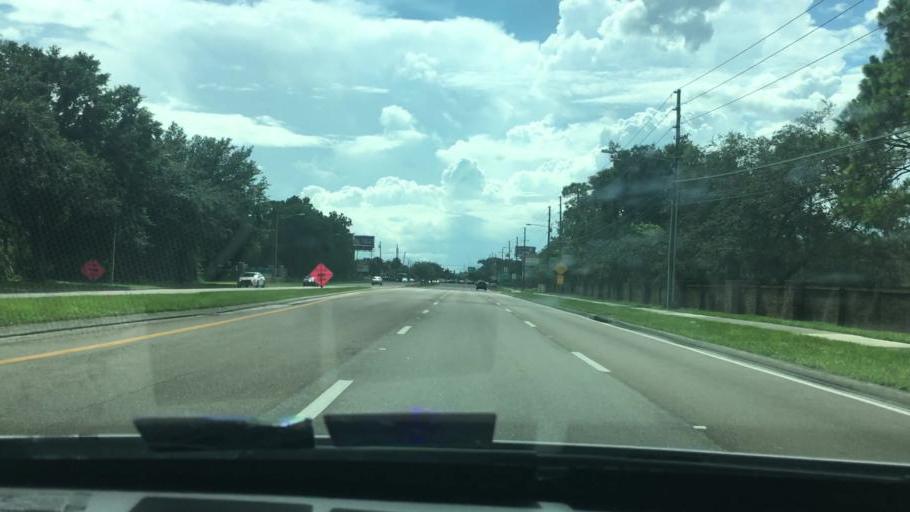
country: US
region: Florida
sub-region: Orange County
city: Alafaya
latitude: 28.5976
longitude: -81.2406
